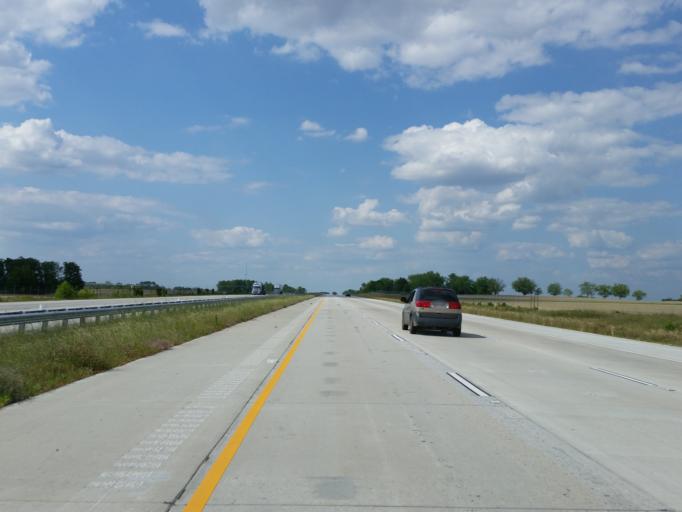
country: US
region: Georgia
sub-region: Dooly County
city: Vienna
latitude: 32.1518
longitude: -83.7559
